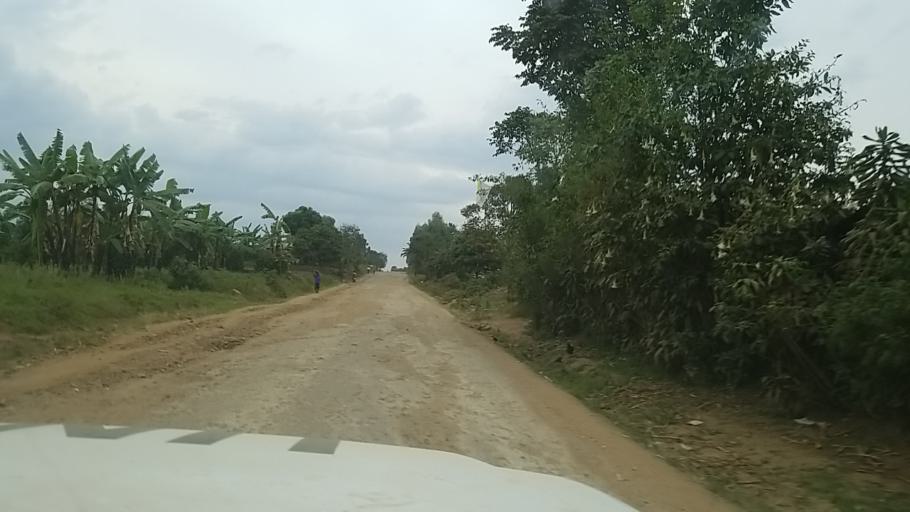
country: CD
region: South Kivu
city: Bukavu
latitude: -2.2651
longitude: 28.8204
